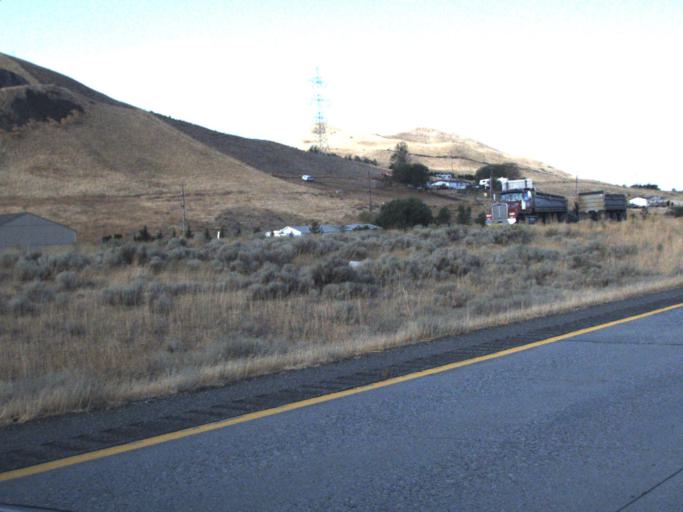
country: US
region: Washington
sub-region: Benton County
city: Benton City
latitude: 46.2656
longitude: -119.5423
